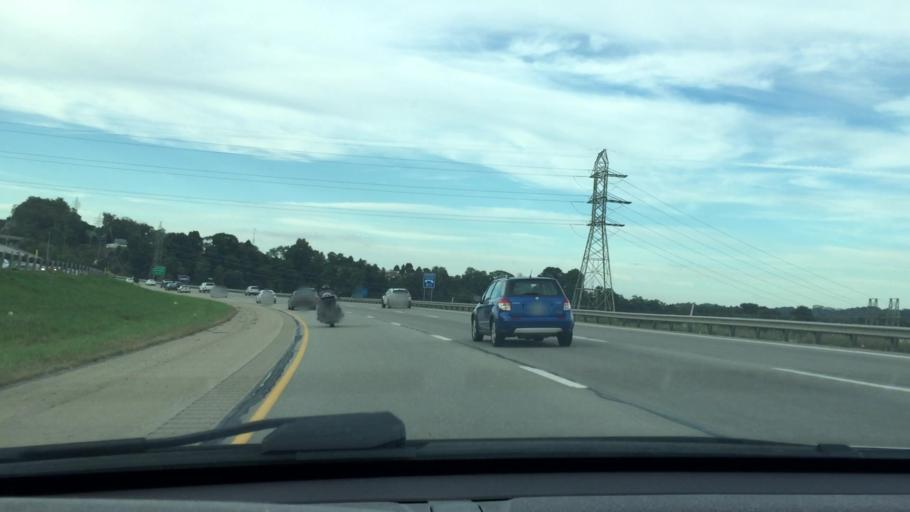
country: US
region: Pennsylvania
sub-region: Allegheny County
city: Heidelberg
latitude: 40.3826
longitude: -80.0963
